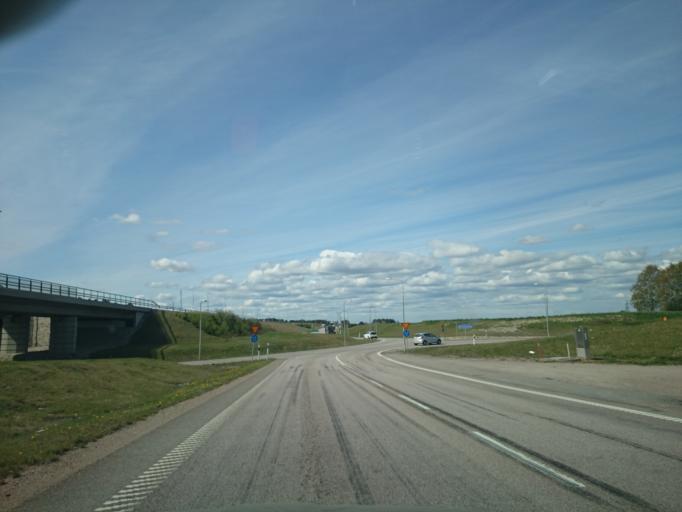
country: SE
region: Uppsala
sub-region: Uppsala Kommun
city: Gamla Uppsala
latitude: 59.8879
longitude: 17.6715
